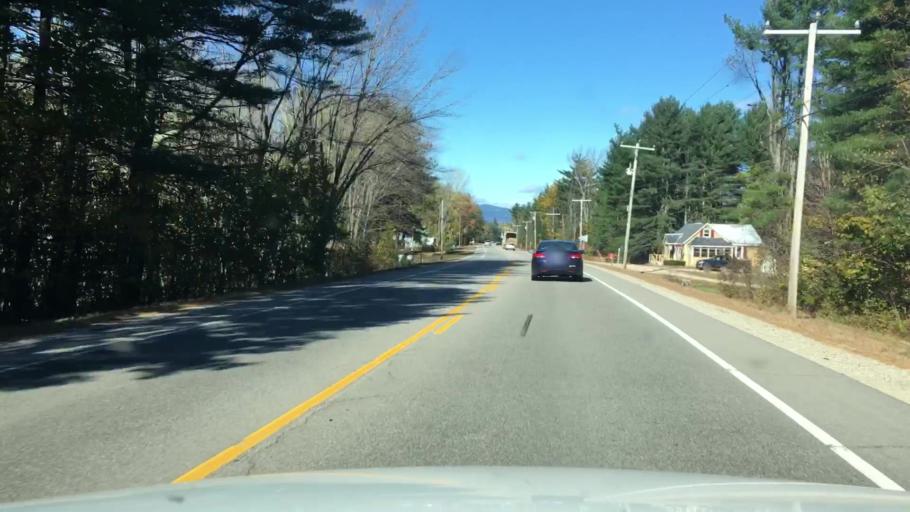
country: US
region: New Hampshire
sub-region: Carroll County
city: Tamworth
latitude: 43.8048
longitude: -71.1825
